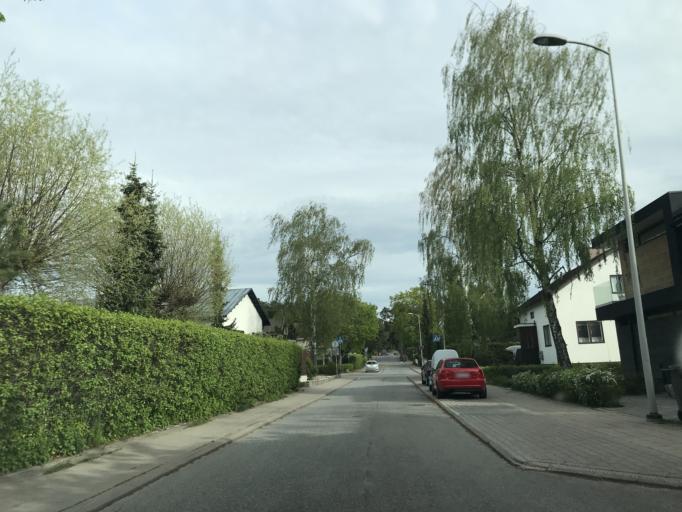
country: FI
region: Varsinais-Suomi
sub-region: Turku
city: Turku
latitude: 60.4389
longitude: 22.2989
